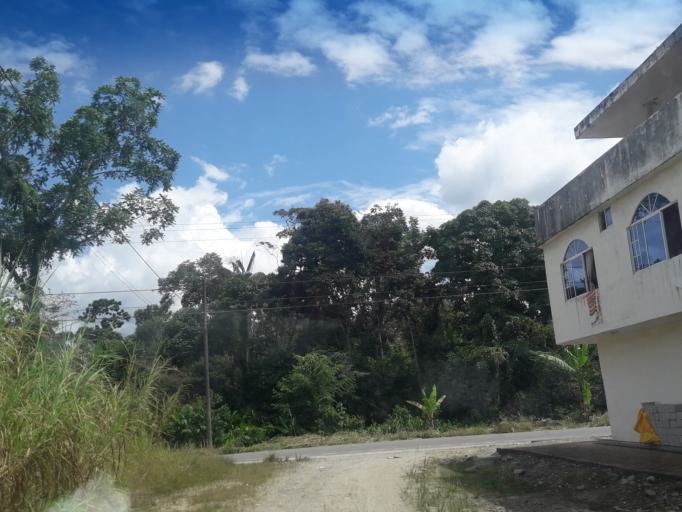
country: EC
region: Napo
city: Tena
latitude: -1.0175
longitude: -77.8622
